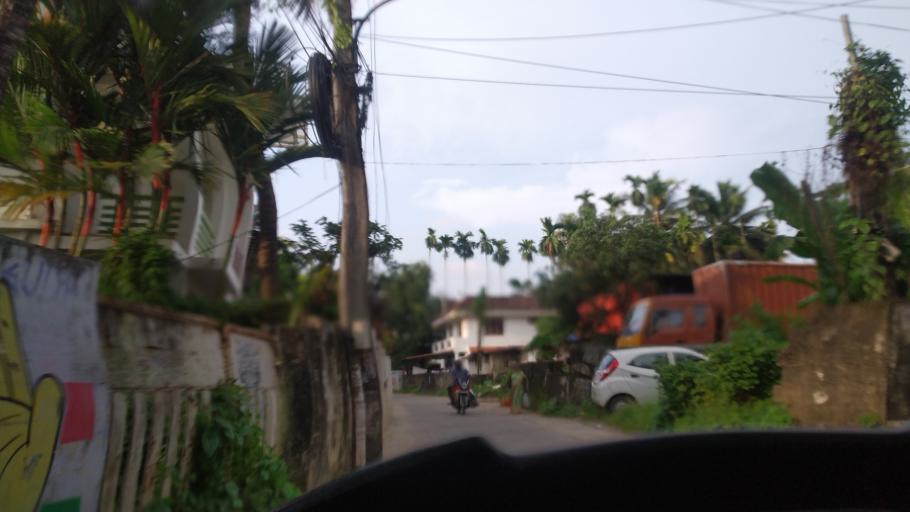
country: IN
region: Kerala
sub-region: Ernakulam
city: Cochin
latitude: 9.9848
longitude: 76.3090
